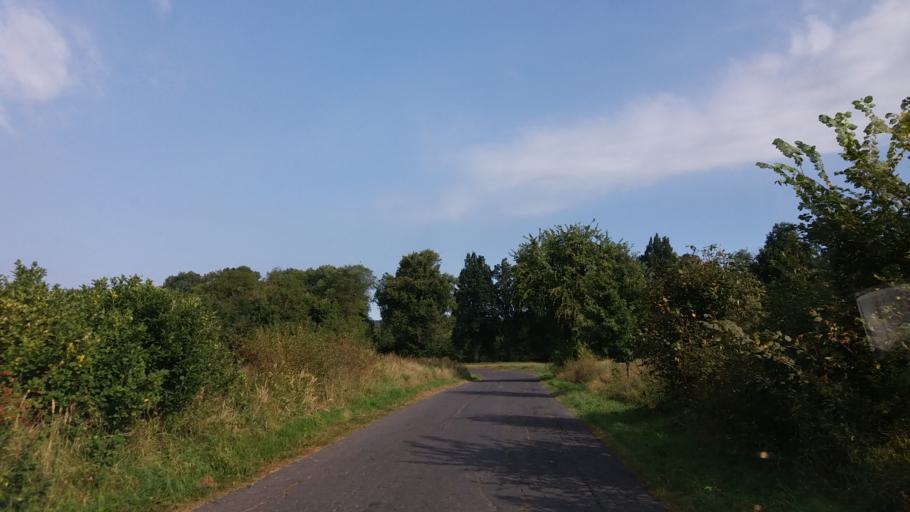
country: PL
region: West Pomeranian Voivodeship
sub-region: Powiat stargardzki
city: Suchan
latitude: 53.2222
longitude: 15.3419
